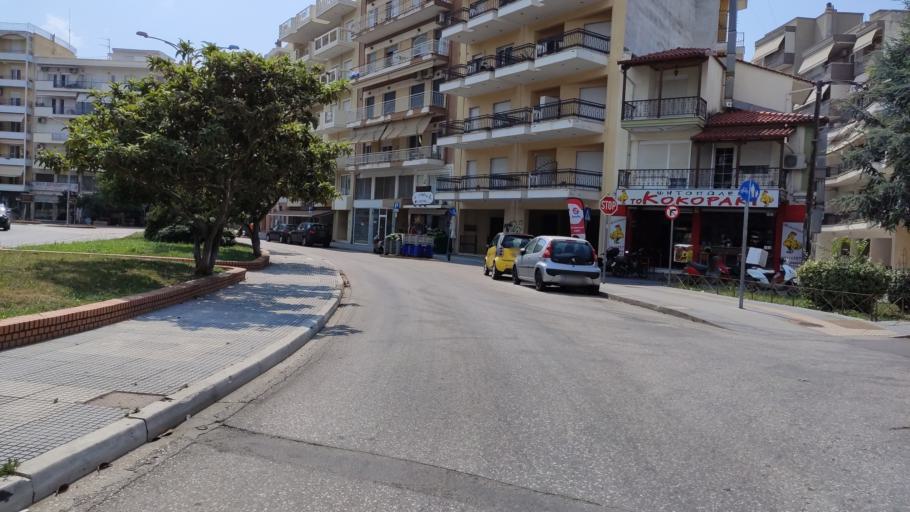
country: GR
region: East Macedonia and Thrace
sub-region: Nomos Rodopis
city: Komotini
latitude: 41.1199
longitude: 25.3987
